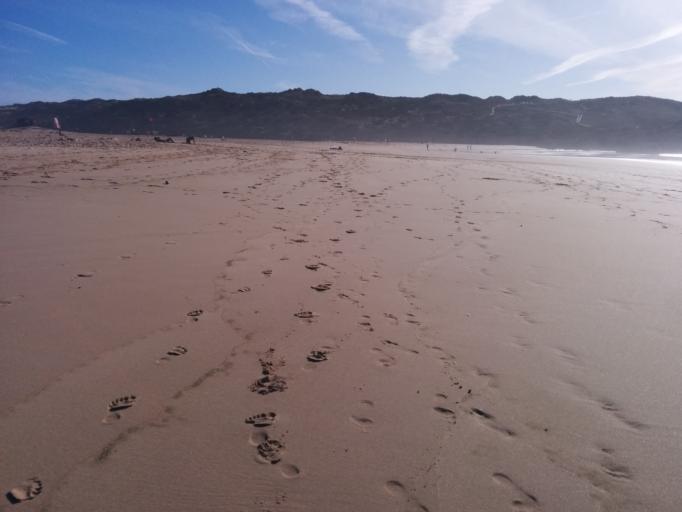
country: PT
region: Faro
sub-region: Vila do Bispo
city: Vila do Bispo
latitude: 37.1995
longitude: -8.9022
